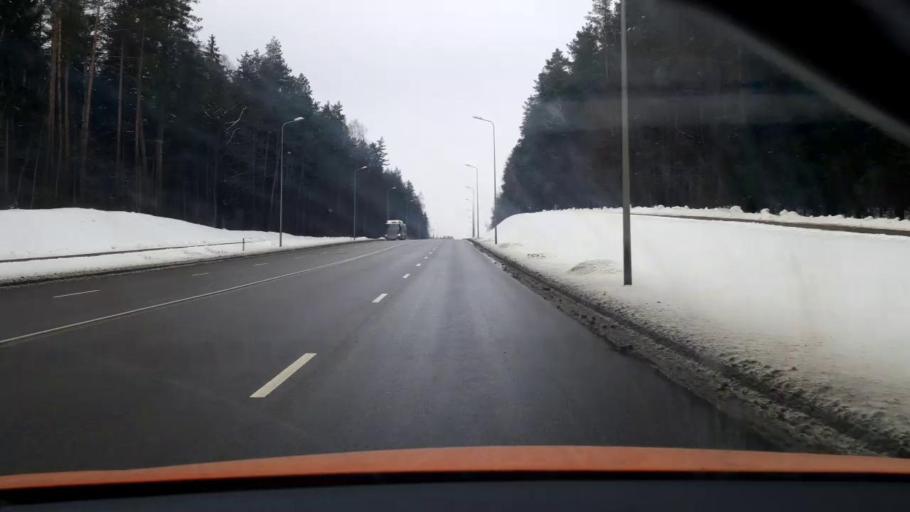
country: LT
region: Vilnius County
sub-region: Vilnius
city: Fabijoniskes
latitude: 54.7605
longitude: 25.2720
